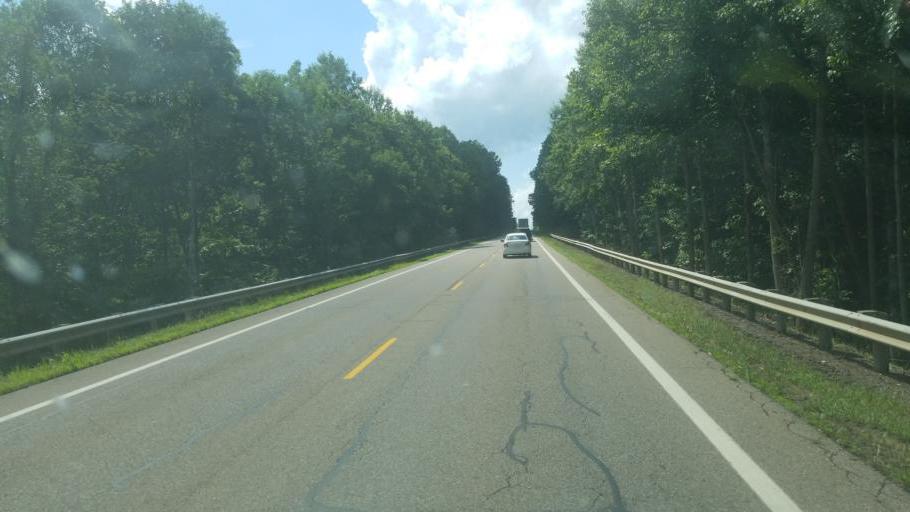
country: US
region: Ohio
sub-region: Knox County
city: Gambier
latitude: 40.3803
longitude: -82.4140
